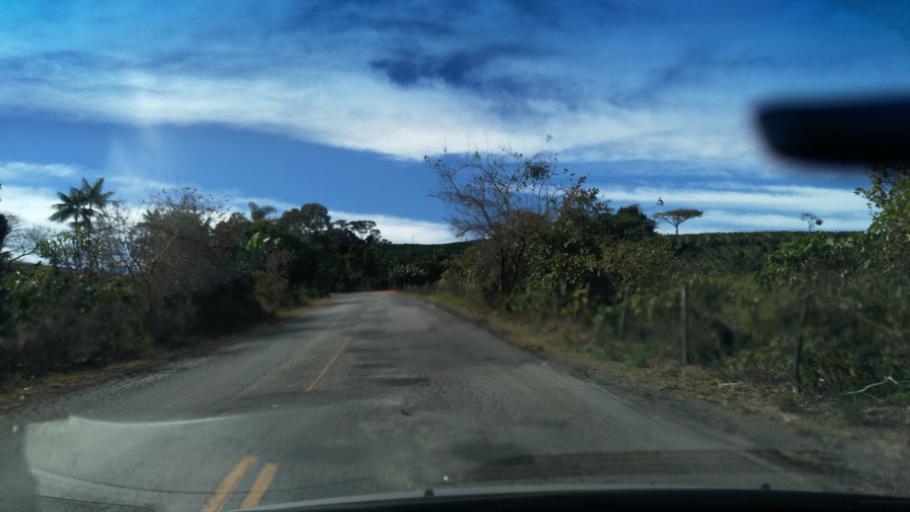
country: BR
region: Minas Gerais
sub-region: Andradas
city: Andradas
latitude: -22.0596
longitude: -46.3701
